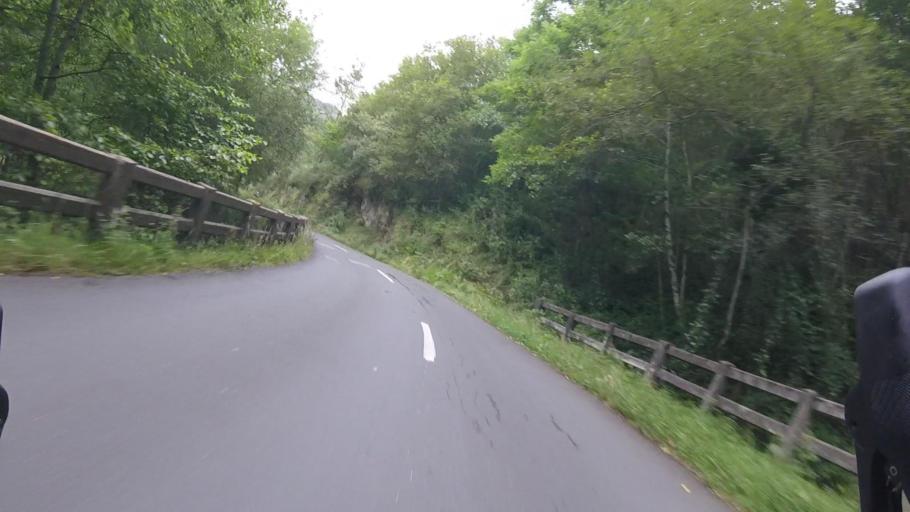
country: ES
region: Basque Country
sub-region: Provincia de Guipuzcoa
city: Irun
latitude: 43.2781
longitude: -1.8194
